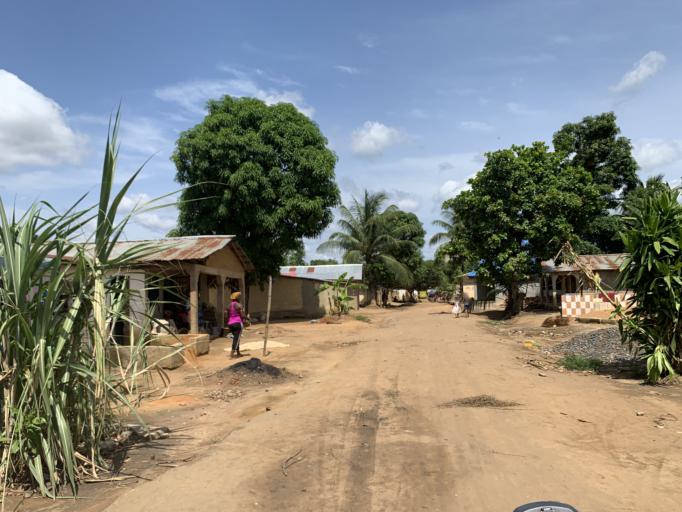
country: SL
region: Western Area
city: Waterloo
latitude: 8.3384
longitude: -13.0474
